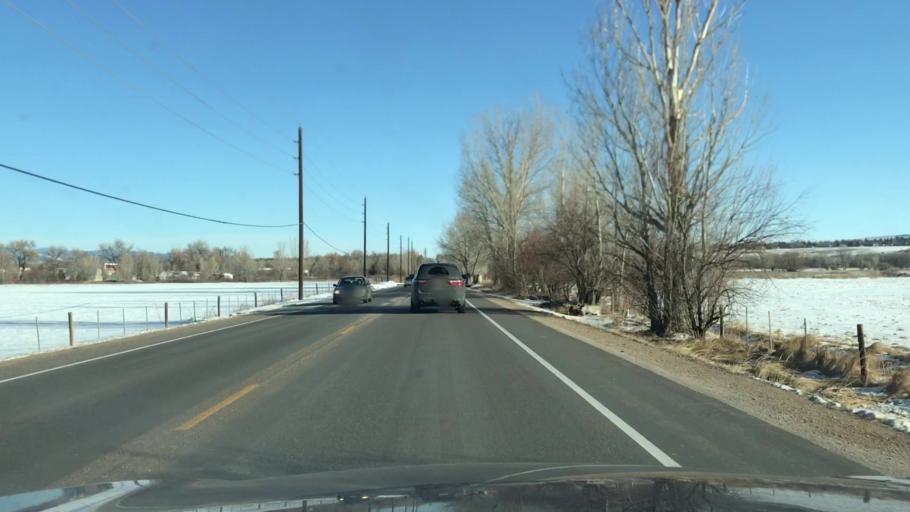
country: US
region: Colorado
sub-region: Boulder County
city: Gunbarrel
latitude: 40.0377
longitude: -105.1784
